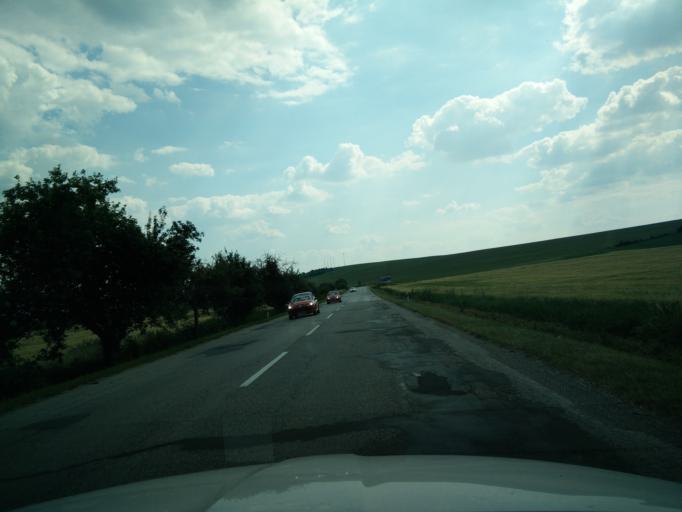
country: SK
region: Nitriansky
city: Partizanske
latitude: 48.6658
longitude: 18.3674
